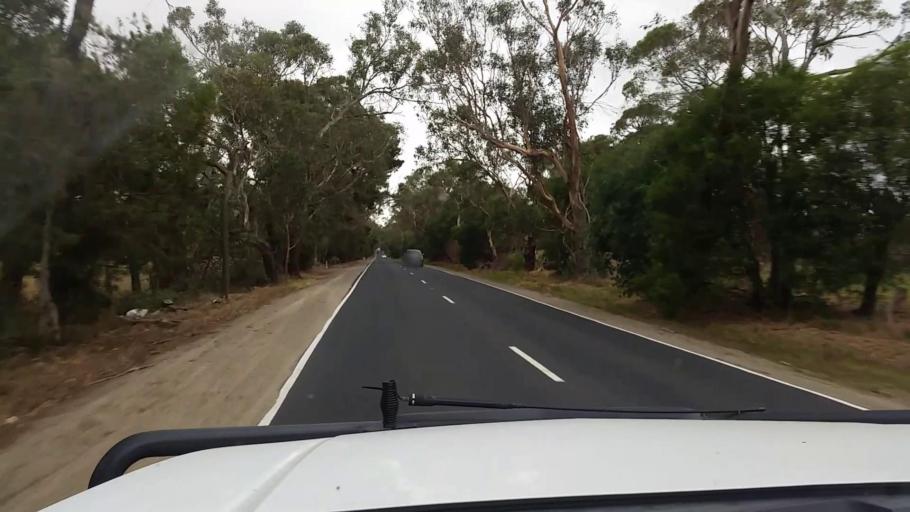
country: AU
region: Victoria
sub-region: Mornington Peninsula
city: Somerville
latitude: -38.2329
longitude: 145.1519
